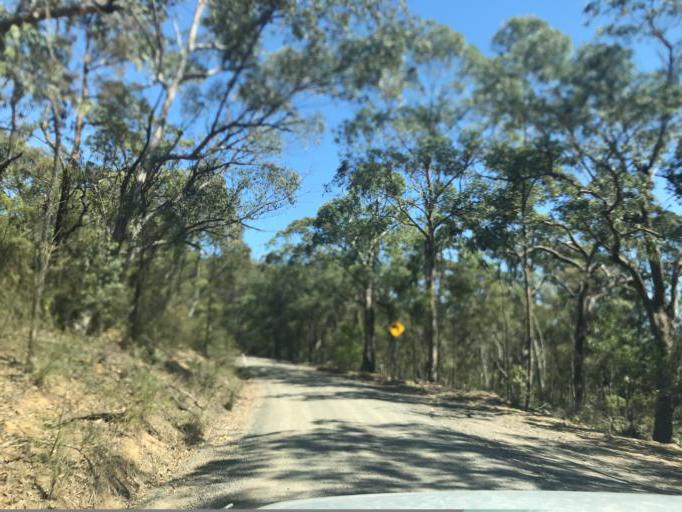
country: AU
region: New South Wales
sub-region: Wyong Shire
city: Little Jilliby
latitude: -33.1518
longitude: 151.0804
